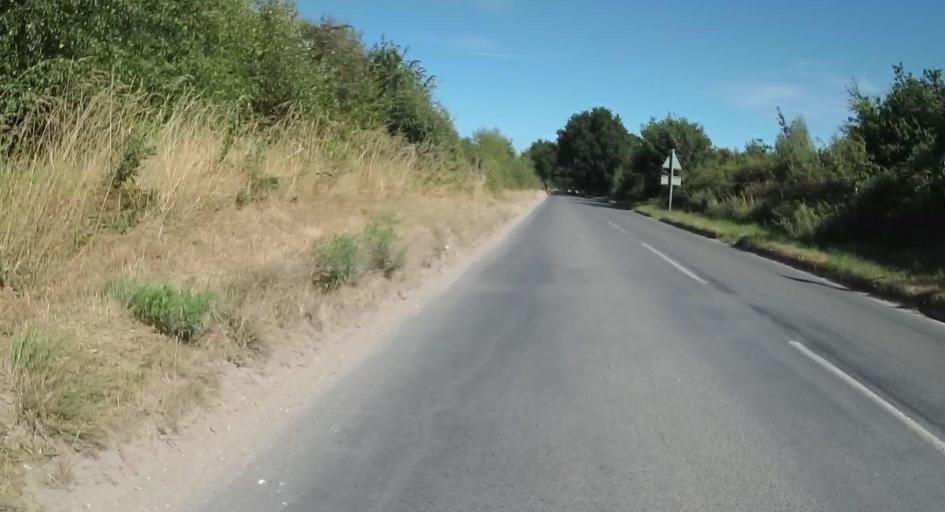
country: GB
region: England
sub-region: Dorset
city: Wareham
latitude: 50.6906
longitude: -2.1651
